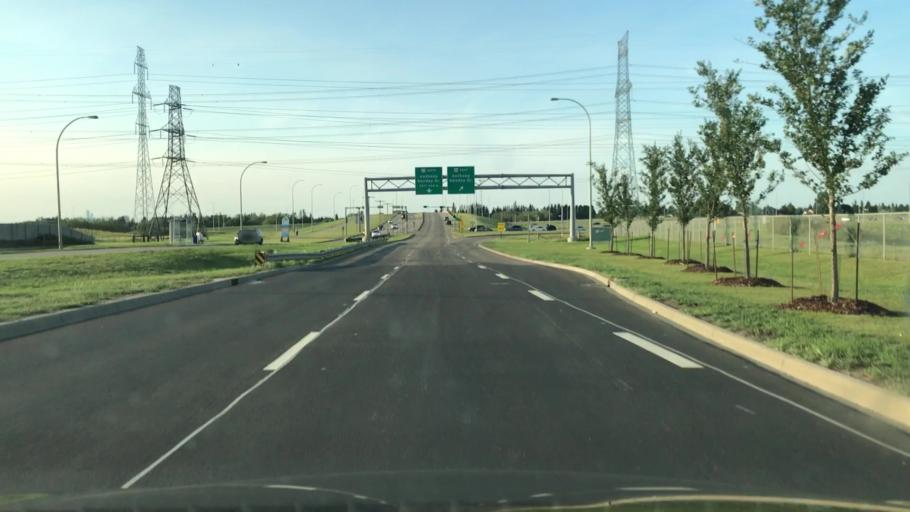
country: CA
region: Alberta
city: Beaumont
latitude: 53.4312
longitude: -113.4177
